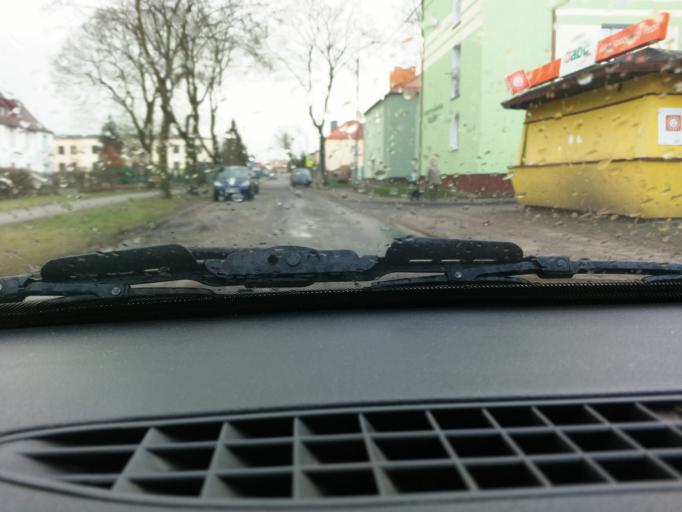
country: PL
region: Kujawsko-Pomorskie
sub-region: Grudziadz
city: Grudziadz
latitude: 53.4298
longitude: 18.7267
